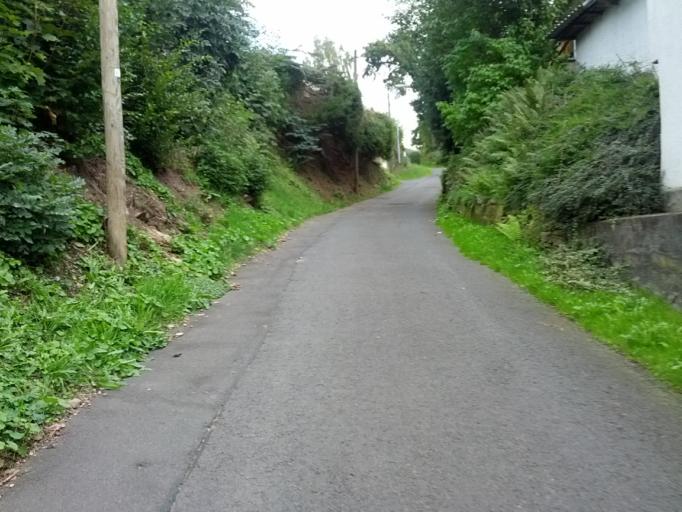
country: DE
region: Thuringia
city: Thal
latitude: 50.9398
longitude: 10.3942
